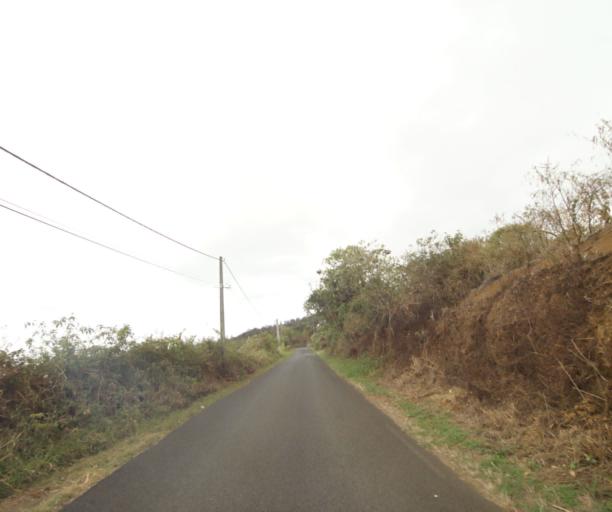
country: RE
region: Reunion
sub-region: Reunion
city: Saint-Paul
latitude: -21.0111
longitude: 55.3397
